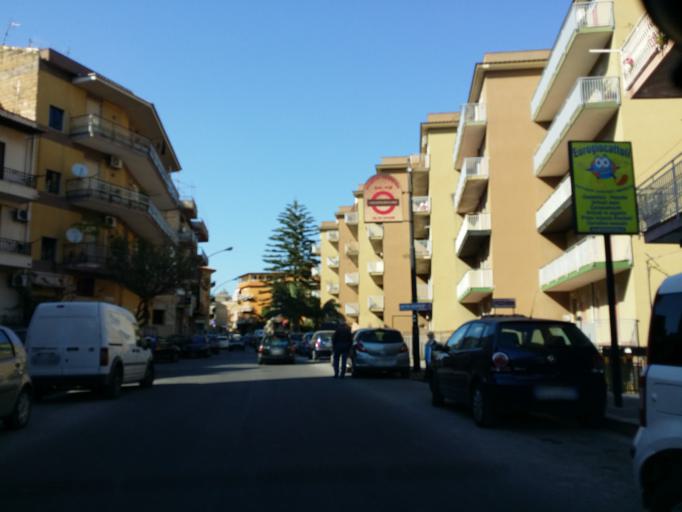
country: IT
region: Sicily
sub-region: Palermo
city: Misilmeri
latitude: 38.0366
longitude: 13.4578
